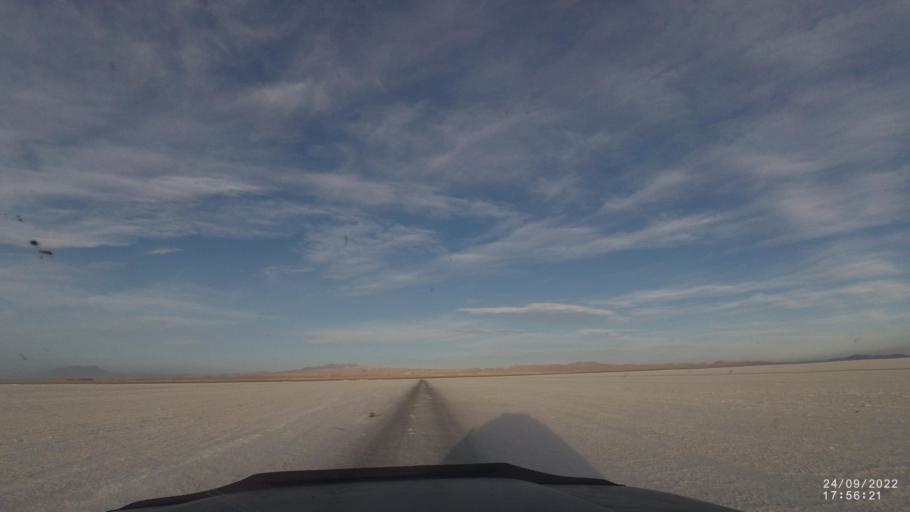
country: BO
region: Potosi
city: Colchani
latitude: -20.3244
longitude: -67.0142
